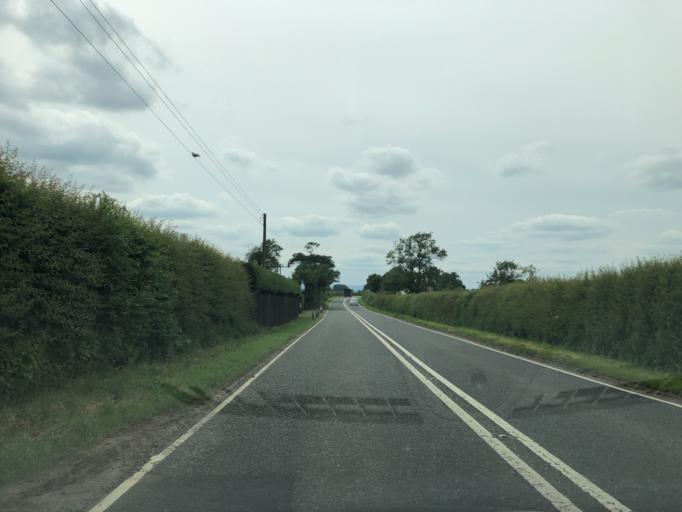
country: GB
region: England
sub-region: North Yorkshire
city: Thirsk
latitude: 54.2320
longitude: -1.2773
